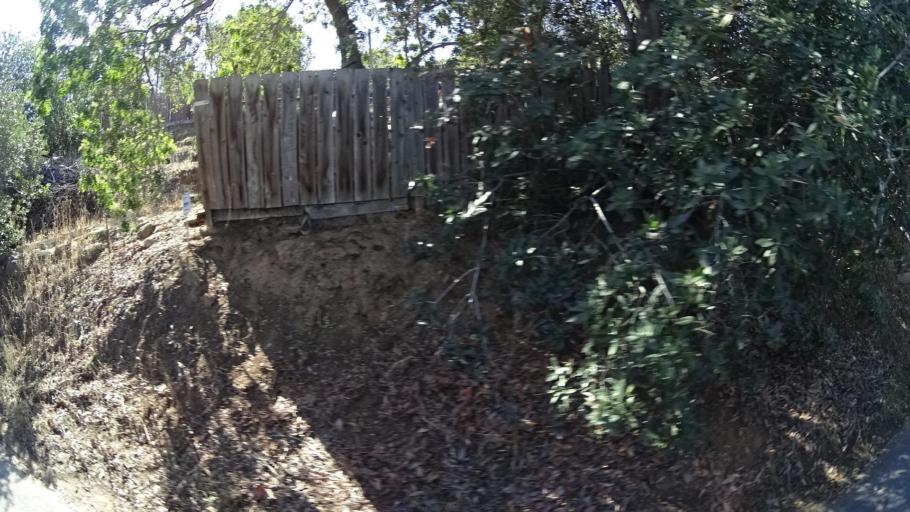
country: US
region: California
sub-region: San Diego County
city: Casa de Oro-Mount Helix
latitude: 32.7759
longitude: -116.9854
